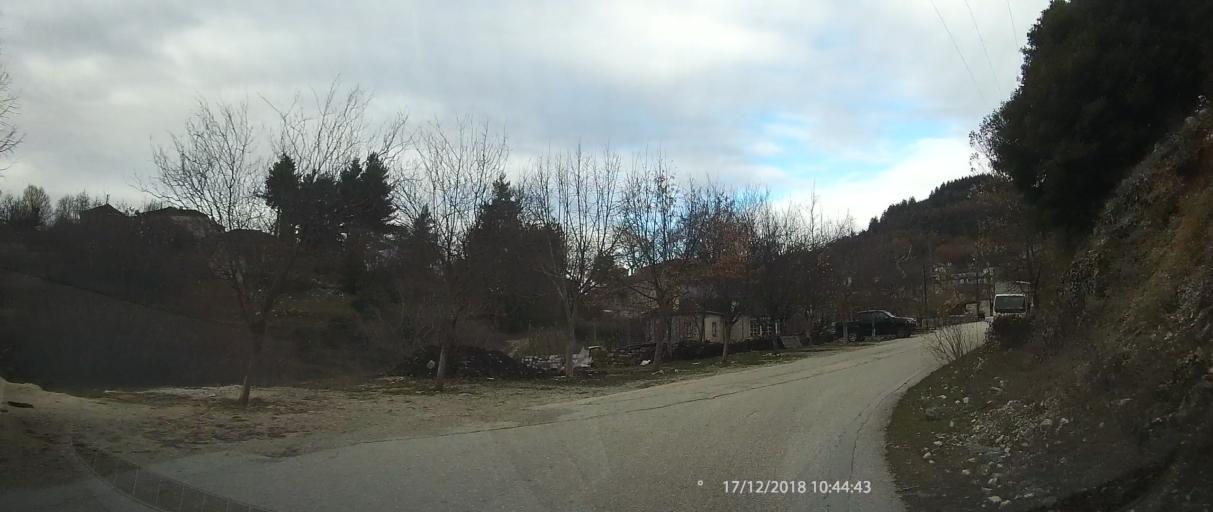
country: GR
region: Epirus
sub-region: Nomos Ioanninon
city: Konitsa
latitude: 39.9673
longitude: 20.7206
